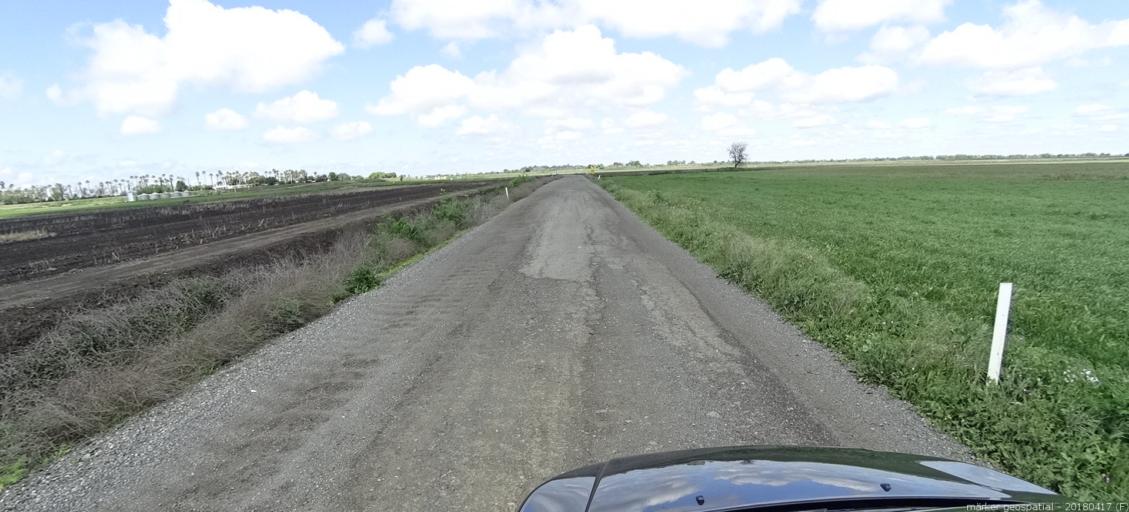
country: US
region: California
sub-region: Solano County
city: Rio Vista
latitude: 38.1442
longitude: -121.5827
